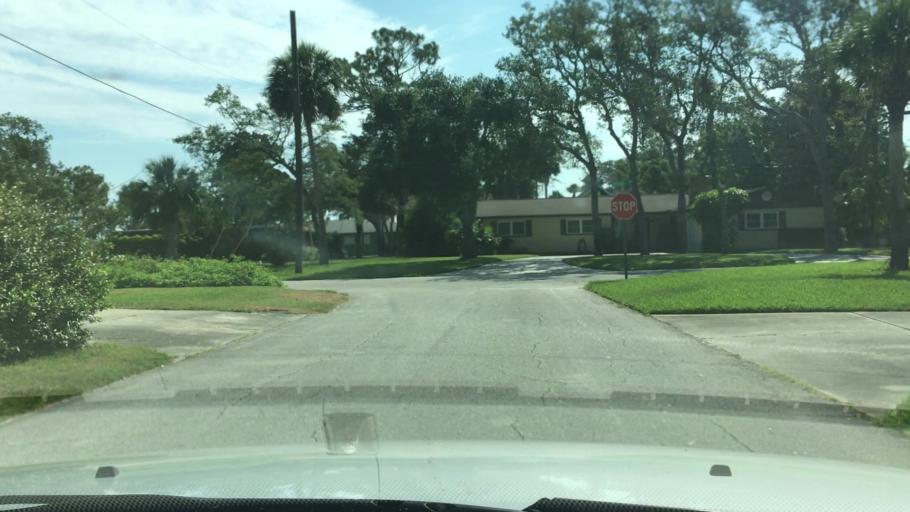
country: US
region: Florida
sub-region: Volusia County
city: Holly Hill
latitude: 29.2606
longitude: -81.0448
